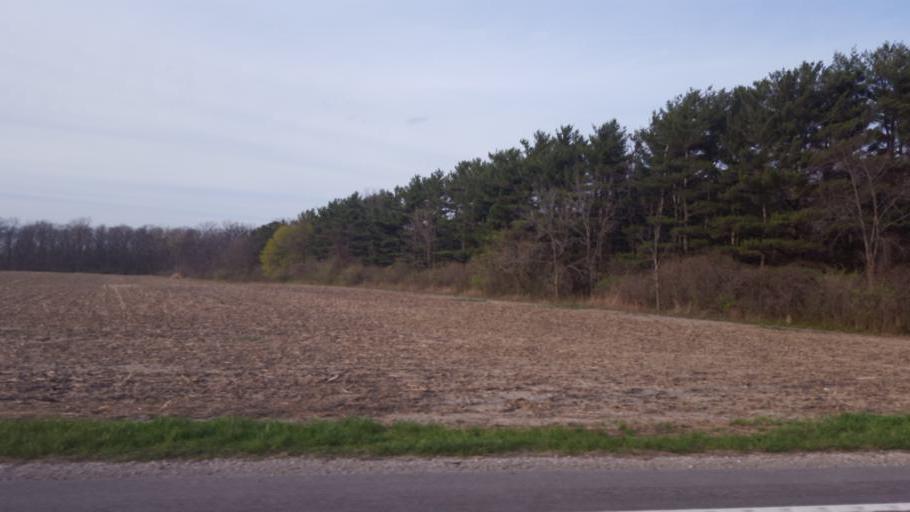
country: US
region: Ohio
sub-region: Erie County
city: Huron
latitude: 41.4085
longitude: -82.6045
